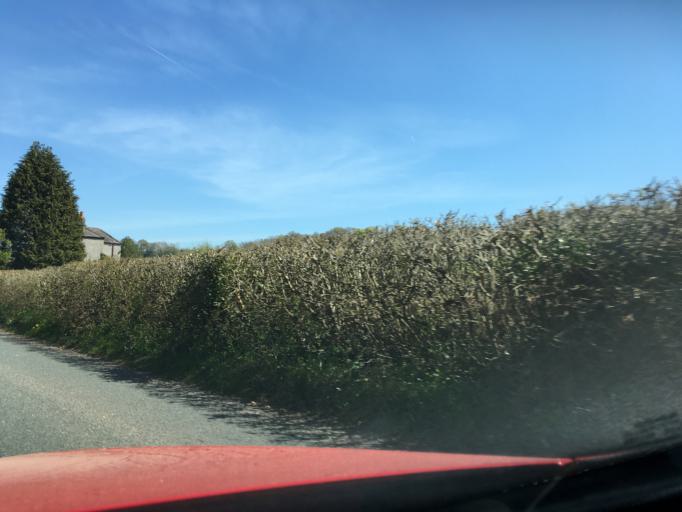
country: GB
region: Wales
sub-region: Monmouthshire
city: Llangwm
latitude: 51.7251
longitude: -2.8338
